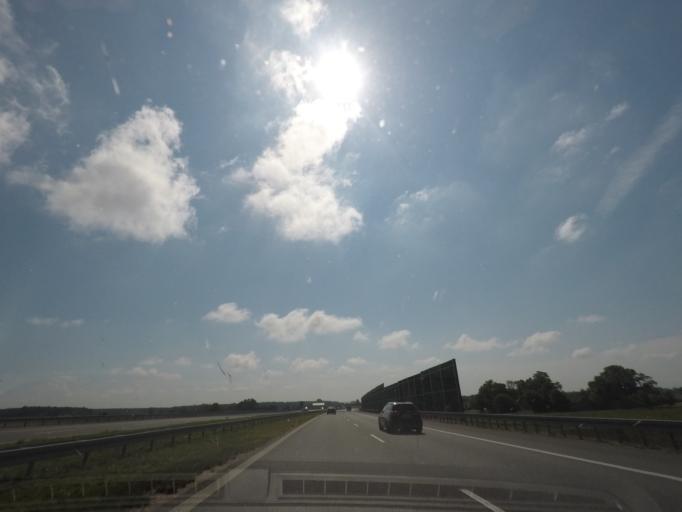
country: PL
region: Kujawsko-Pomorskie
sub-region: Powiat wloclawski
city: Baruchowo
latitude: 52.4539
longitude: 19.2172
